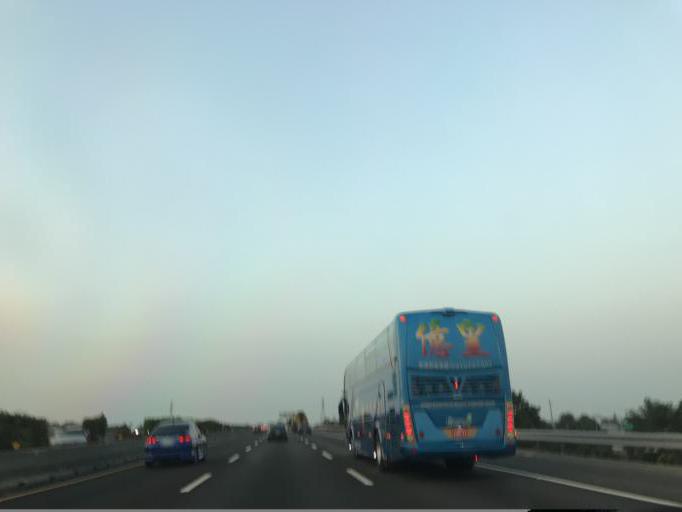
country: TW
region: Taiwan
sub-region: Yunlin
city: Douliu
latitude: 23.7146
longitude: 120.4762
